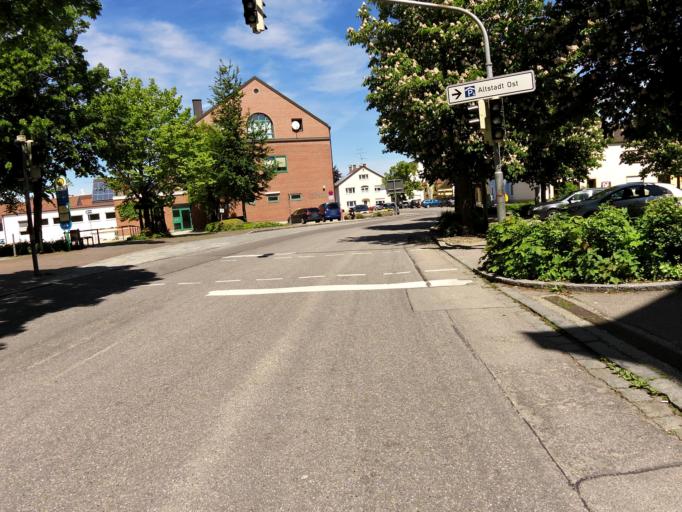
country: DE
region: Bavaria
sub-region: Upper Bavaria
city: Moosburg
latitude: 48.4693
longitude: 11.9376
